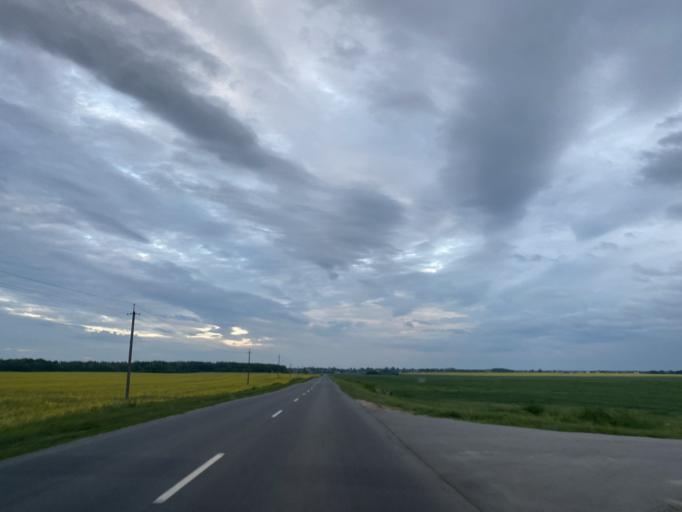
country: BY
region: Minsk
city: Rudzyensk
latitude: 53.6087
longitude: 27.8236
